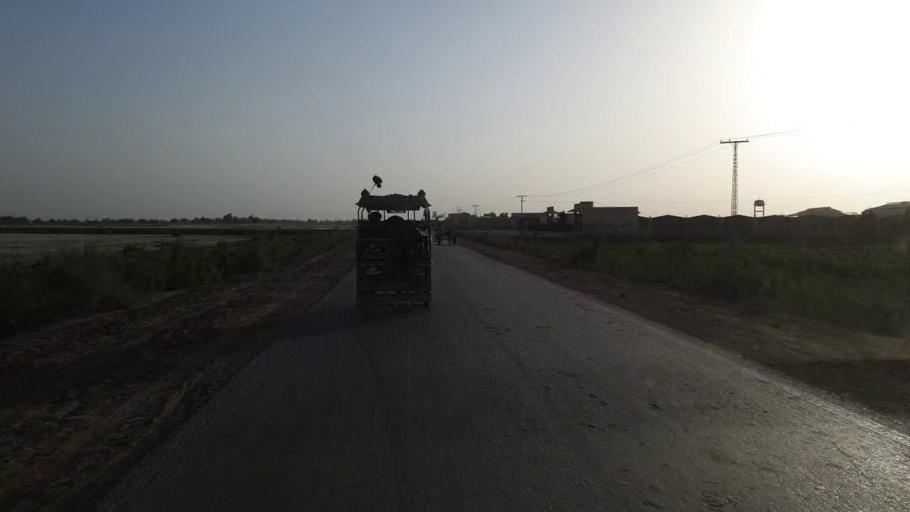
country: PK
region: Sindh
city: Jam Sahib
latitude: 26.2905
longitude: 68.6103
